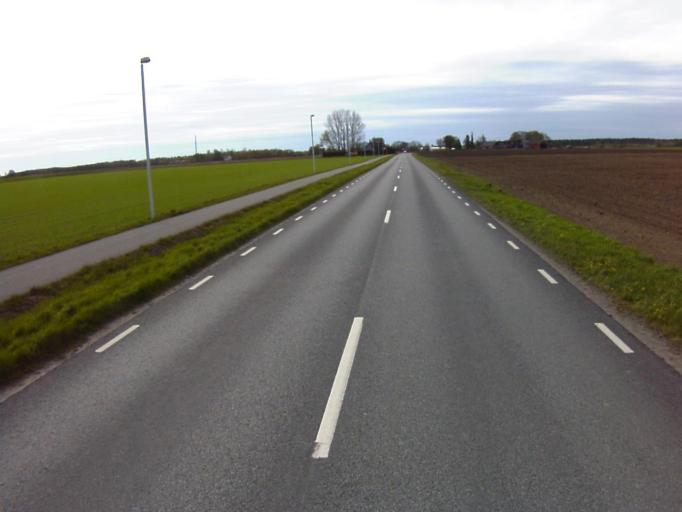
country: SE
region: Skane
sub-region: Kristianstads Kommun
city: Norra Asum
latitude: 56.0080
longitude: 14.1286
